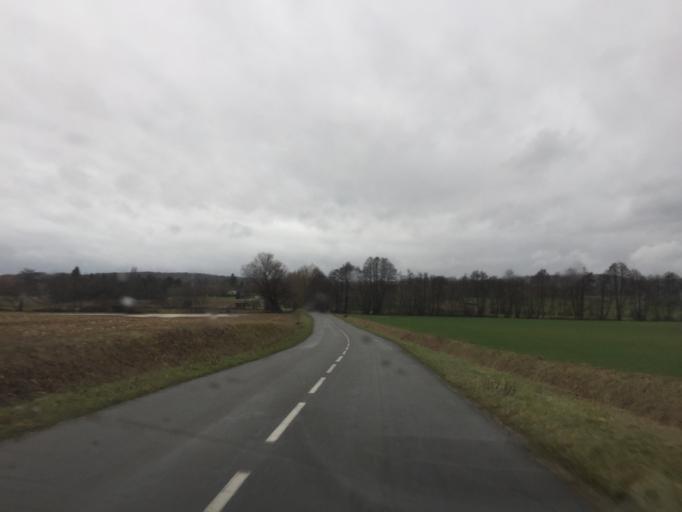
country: FR
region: Franche-Comte
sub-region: Departement du Jura
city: Dole
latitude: 47.1452
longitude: 5.5622
